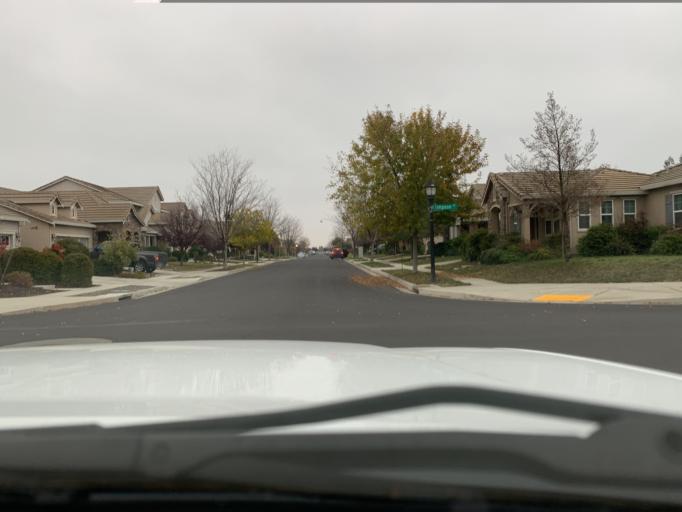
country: US
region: California
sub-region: Yolo County
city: Woodland
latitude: 38.6461
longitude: -121.7425
